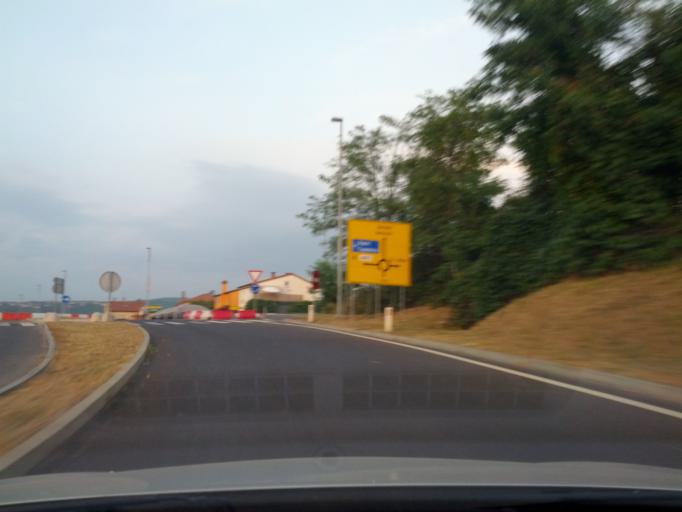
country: SI
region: Koper-Capodistria
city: Prade
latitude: 45.5459
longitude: 13.7634
